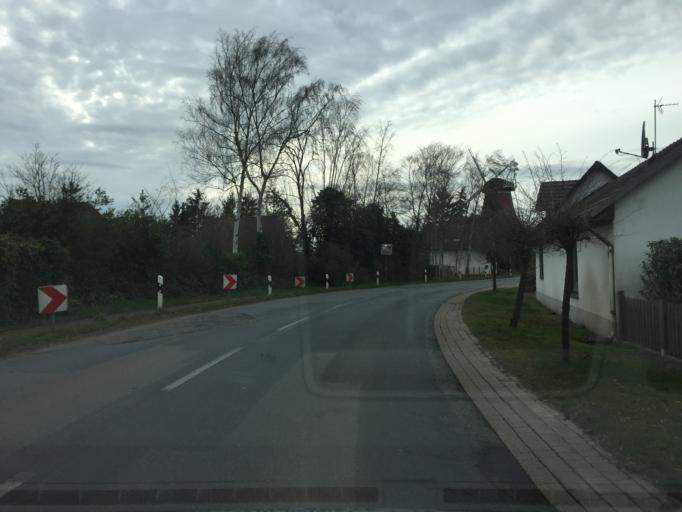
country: DE
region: Lower Saxony
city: Emtinghausen
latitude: 52.9326
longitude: 8.9697
